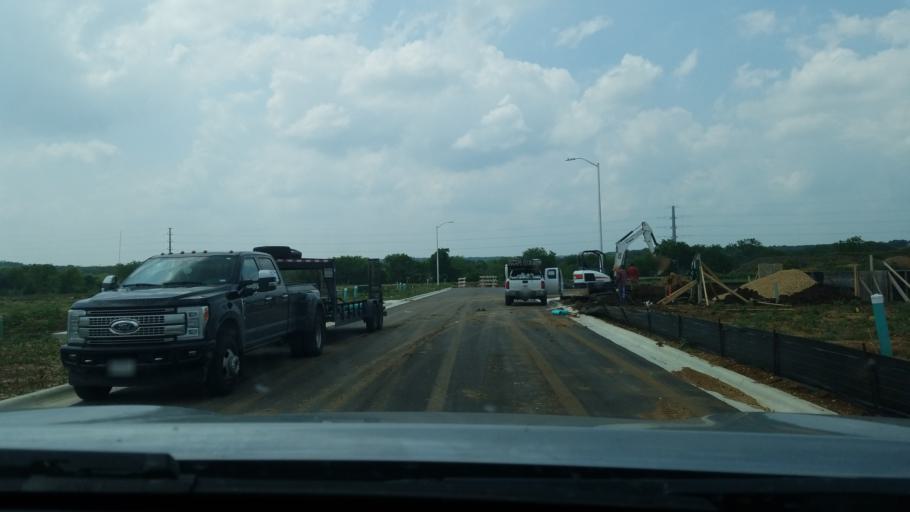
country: US
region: Texas
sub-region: Comal County
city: New Braunfels
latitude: 29.7486
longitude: -98.0941
